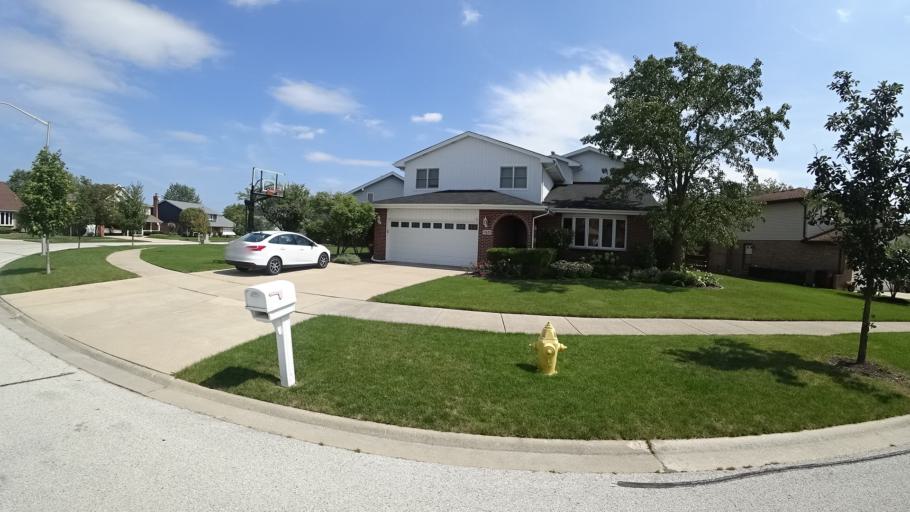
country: US
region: Illinois
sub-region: Cook County
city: Orland Hills
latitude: 41.5701
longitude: -87.8216
